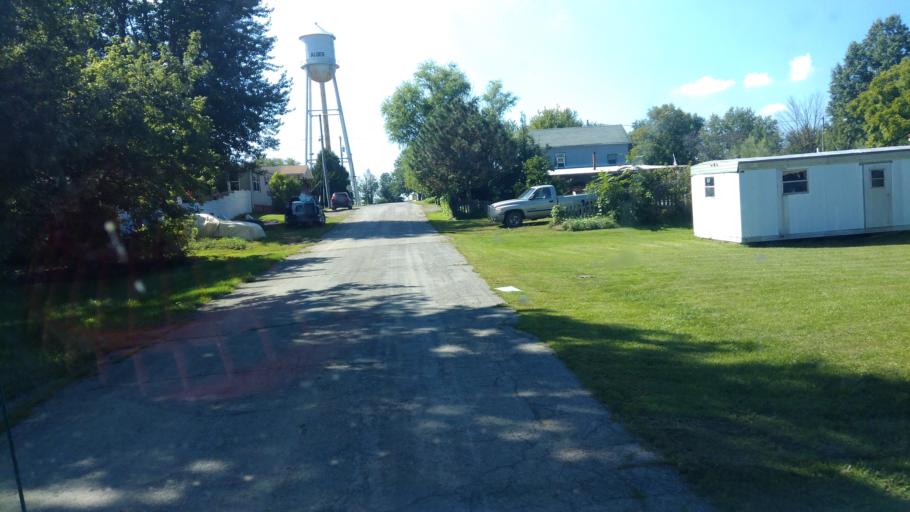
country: US
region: Ohio
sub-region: Hardin County
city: Ada
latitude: 40.7132
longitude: -83.8443
